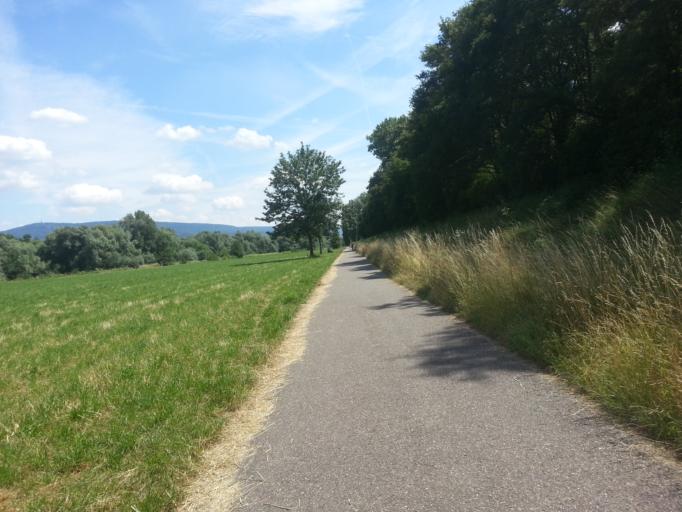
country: DE
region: Baden-Wuerttemberg
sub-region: Karlsruhe Region
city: Dossenheim
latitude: 49.4354
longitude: 8.6454
